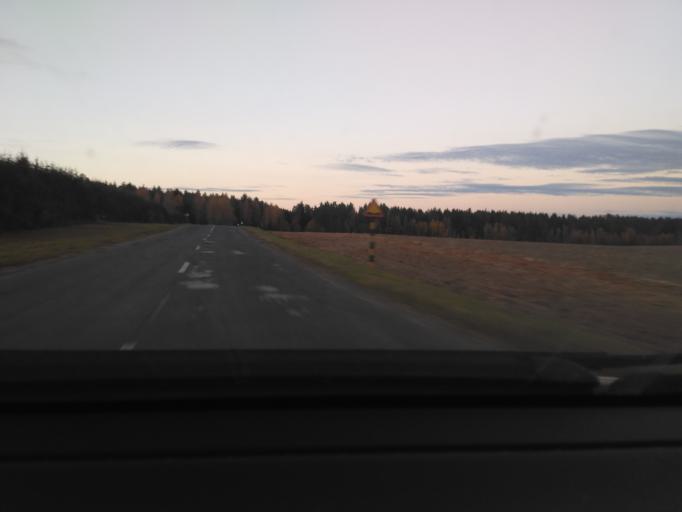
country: BY
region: Minsk
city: Loshnitsa
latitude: 54.3678
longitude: 28.6235
